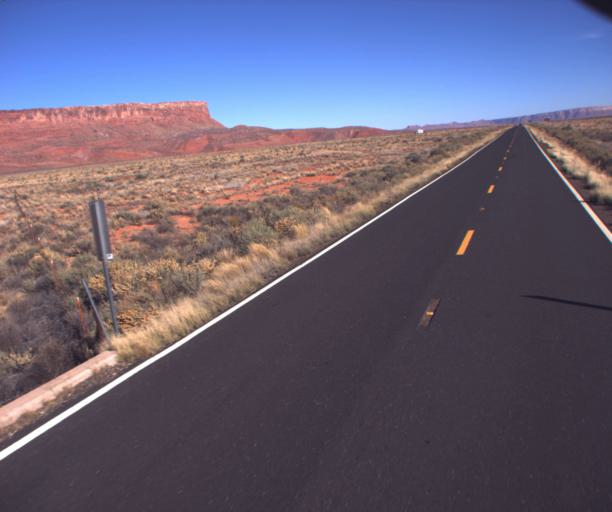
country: US
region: Arizona
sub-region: Coconino County
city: Page
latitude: 36.6975
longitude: -111.9153
